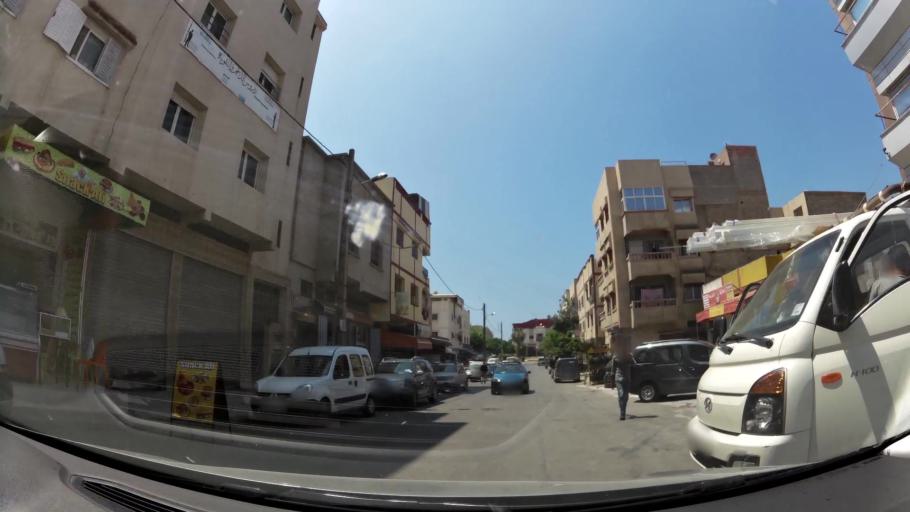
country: MA
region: Rabat-Sale-Zemmour-Zaer
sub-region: Skhirate-Temara
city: Temara
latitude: 33.9730
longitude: -6.8904
